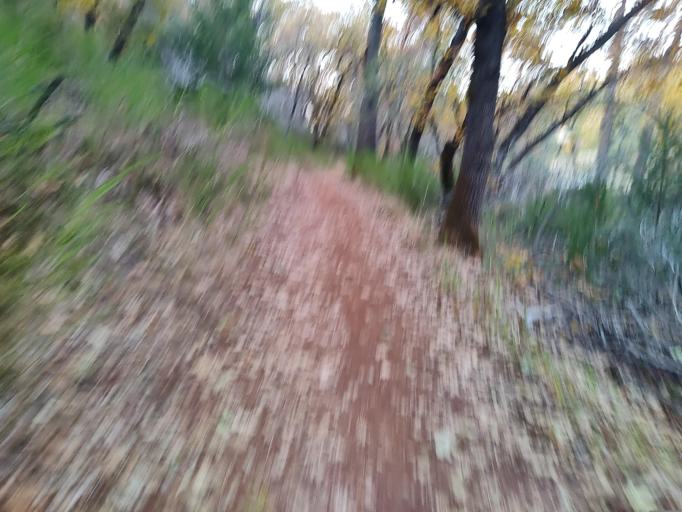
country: US
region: California
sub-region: Placer County
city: Meadow Vista
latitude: 39.0334
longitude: -120.9813
